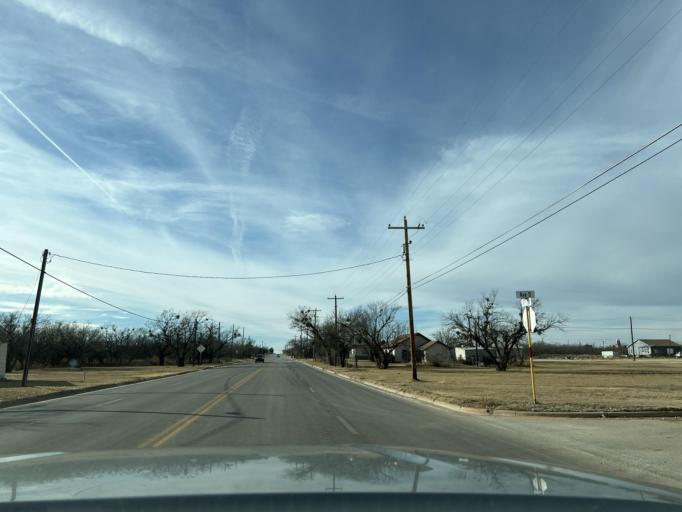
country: US
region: Texas
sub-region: Jones County
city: Anson
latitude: 32.7515
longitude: -99.8883
